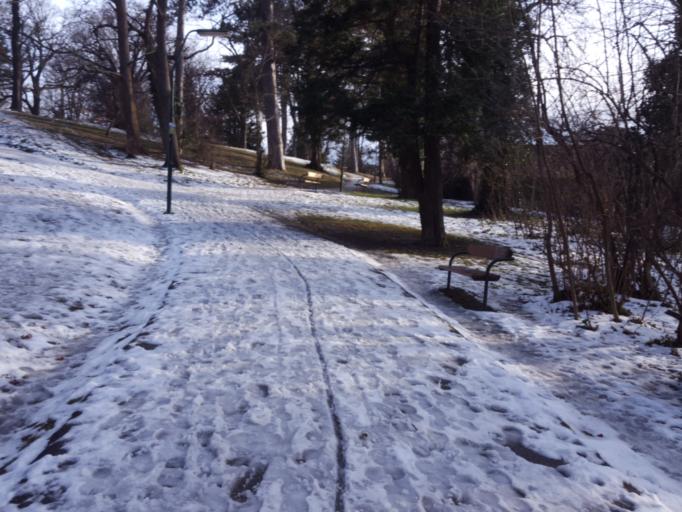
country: AT
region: Lower Austria
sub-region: Politischer Bezirk Modling
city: Perchtoldsdorf
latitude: 48.1789
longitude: 16.3000
